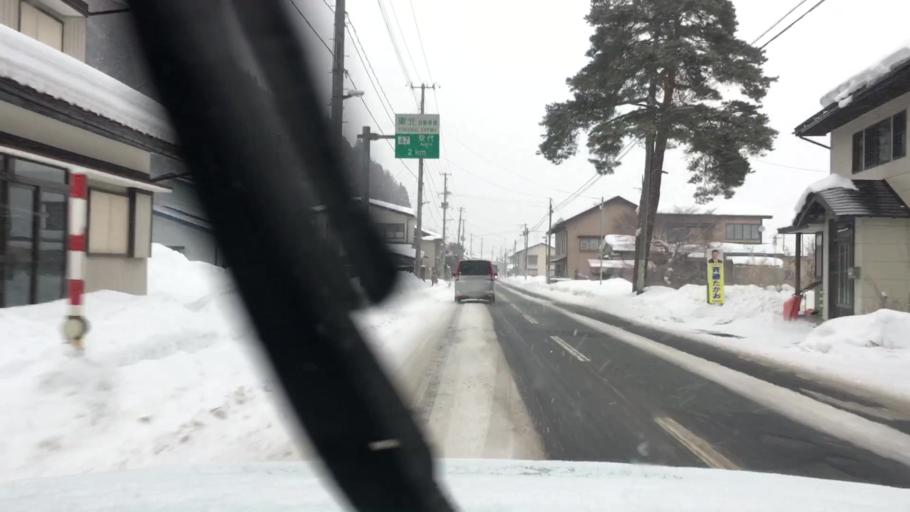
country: JP
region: Iwate
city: Ichinohe
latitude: 40.0931
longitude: 141.0470
